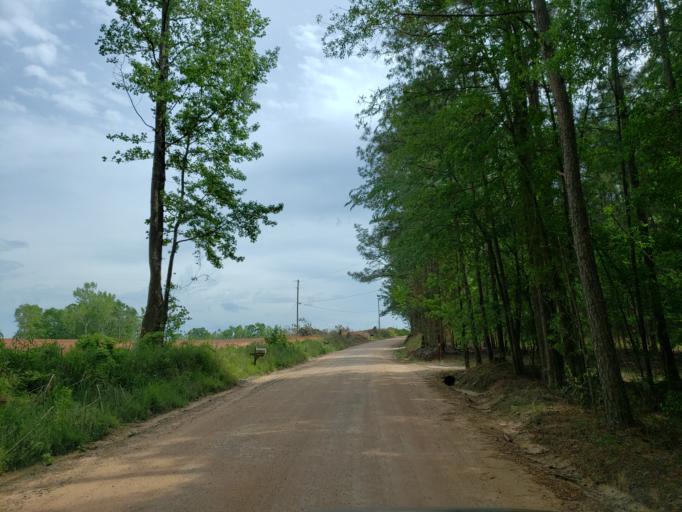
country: US
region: Georgia
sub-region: Monroe County
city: Forsyth
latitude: 32.9830
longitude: -83.9137
